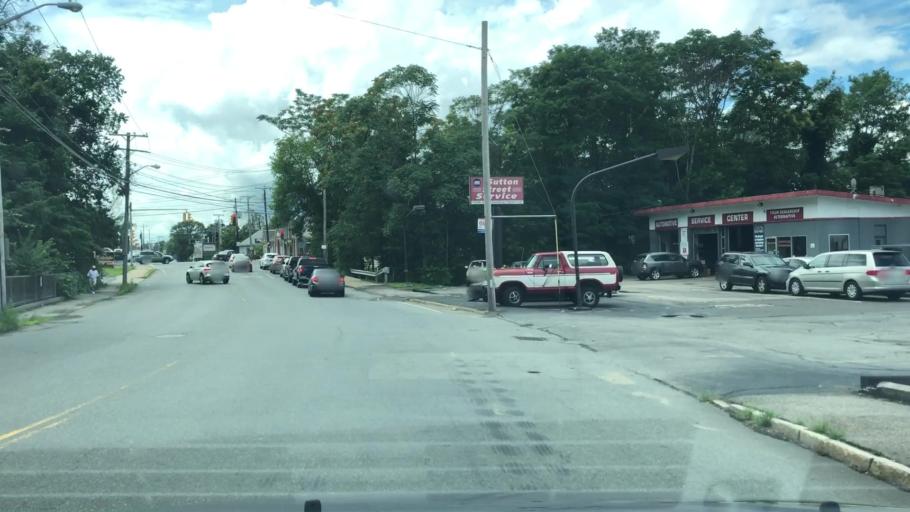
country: US
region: Massachusetts
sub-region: Essex County
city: North Andover
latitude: 42.7070
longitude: -71.1321
